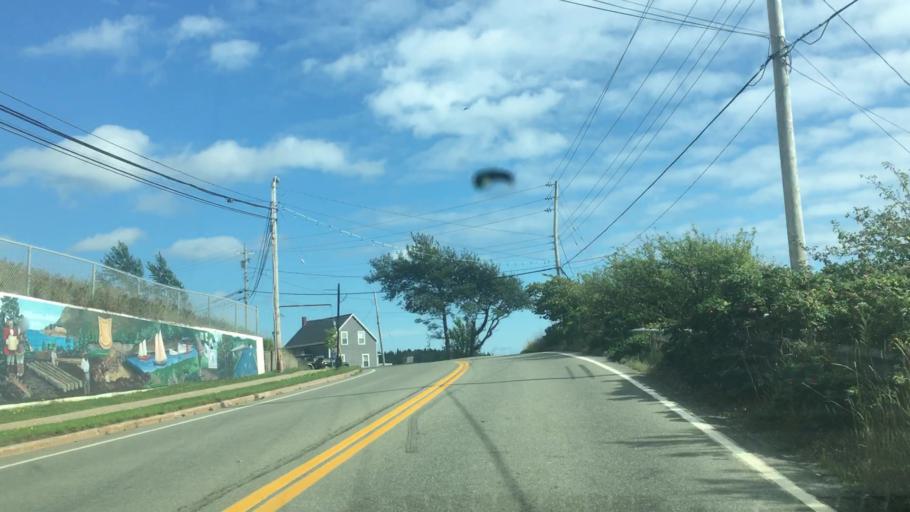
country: CA
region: Nova Scotia
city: Princeville
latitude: 45.6556
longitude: -60.8800
